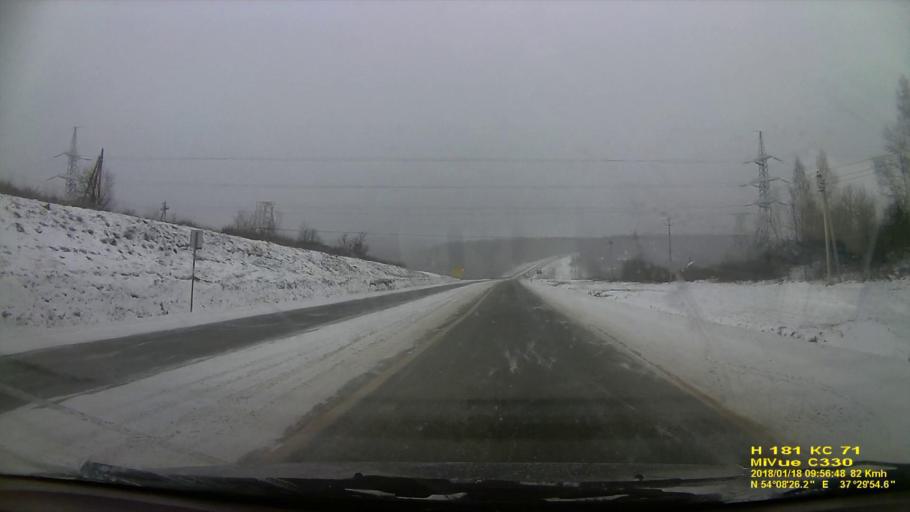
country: RU
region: Tula
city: Kosaya Gora
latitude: 54.1405
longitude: 37.4985
